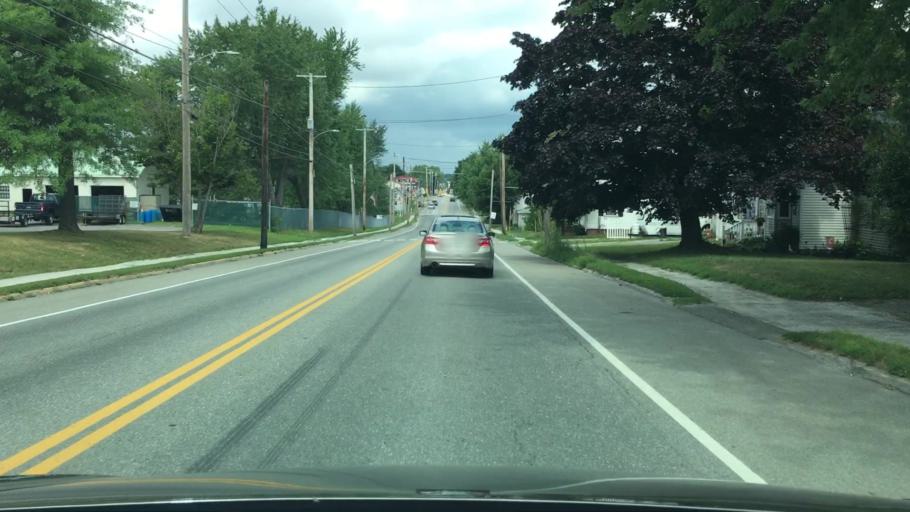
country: US
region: Maine
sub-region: Penobscot County
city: Brewer
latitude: 44.7880
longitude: -68.7547
